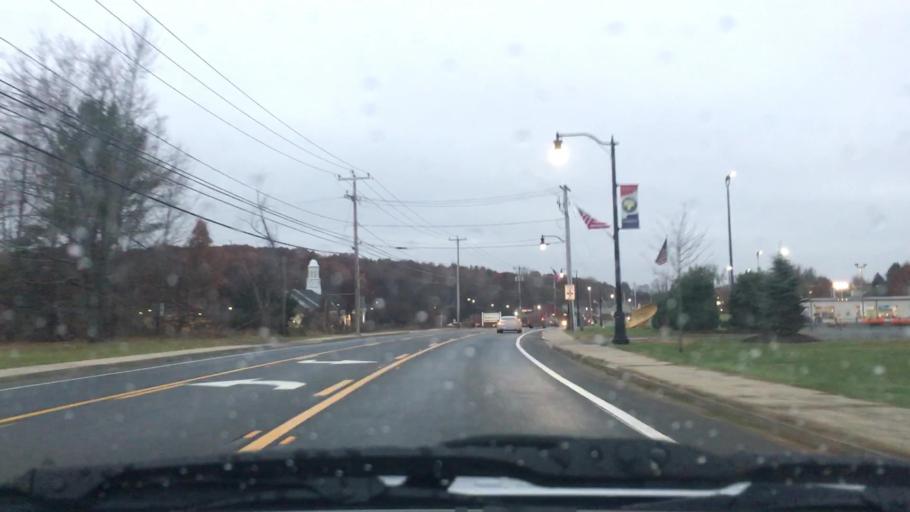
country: US
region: Massachusetts
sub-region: Hampden County
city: Southwick
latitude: 42.0704
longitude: -72.7647
